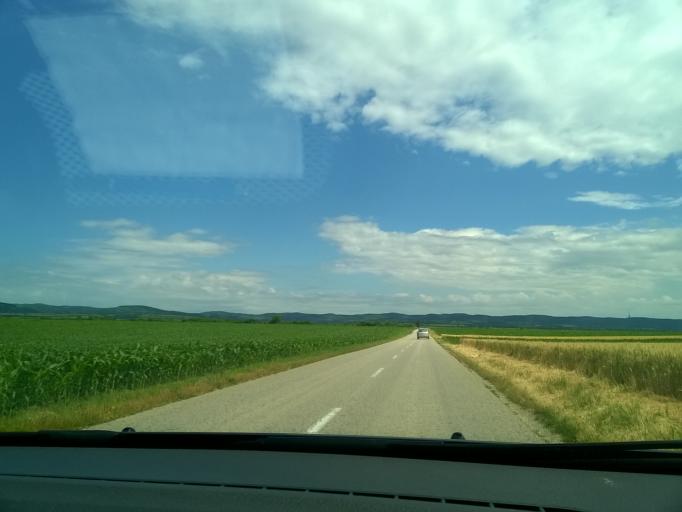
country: RS
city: Vrdnik
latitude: 45.0668
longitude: 19.8088
